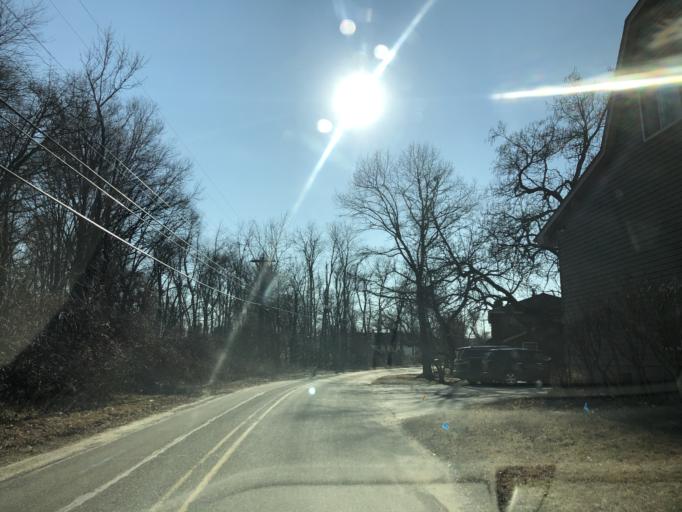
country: US
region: Pennsylvania
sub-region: Delaware County
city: Chester
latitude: 39.8037
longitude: -75.3546
